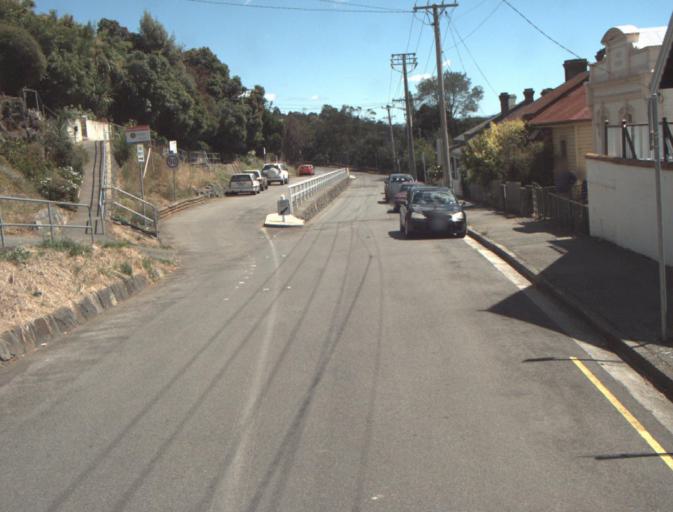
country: AU
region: Tasmania
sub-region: Launceston
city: Launceston
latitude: -41.4429
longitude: 147.1318
